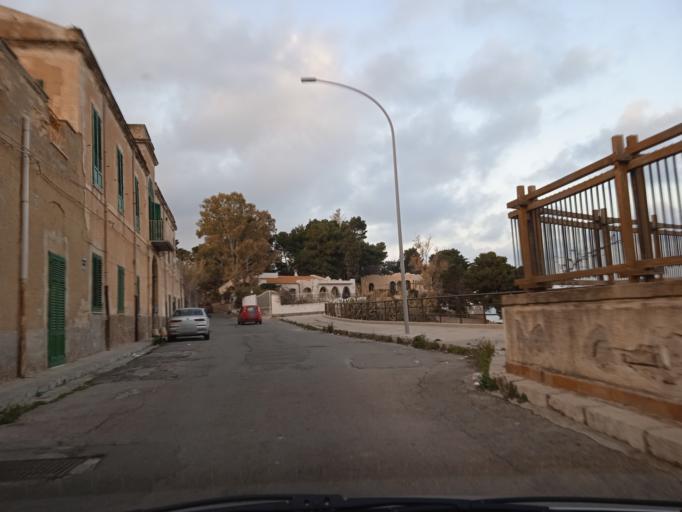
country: IT
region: Sicily
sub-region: Palermo
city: Santa Flavia
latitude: 38.0926
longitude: 13.5397
